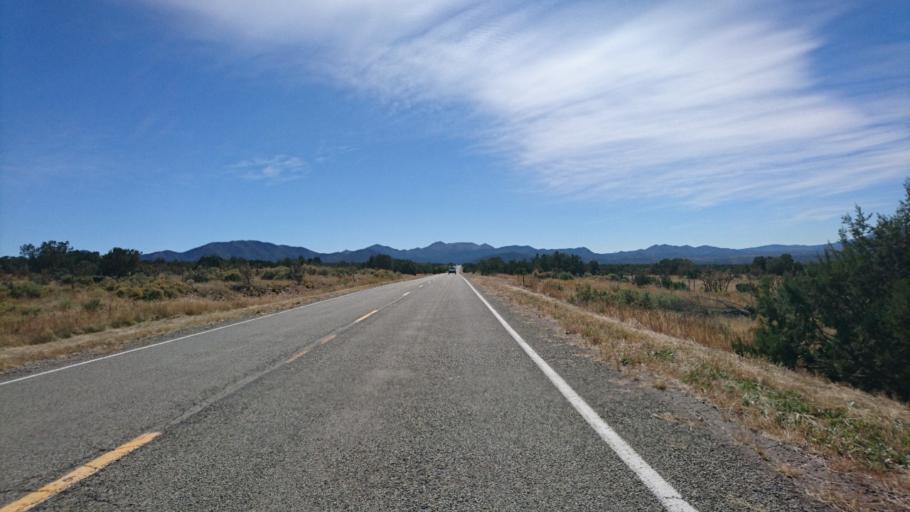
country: US
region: New Mexico
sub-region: Bernalillo County
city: Sandia Knolls
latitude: 35.3155
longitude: -106.2151
